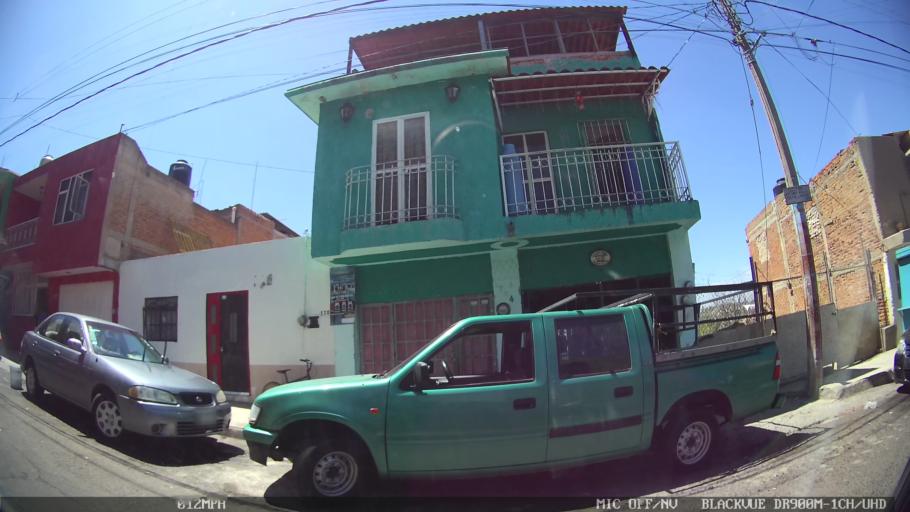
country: MX
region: Jalisco
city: Tlaquepaque
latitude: 20.6876
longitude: -103.2893
